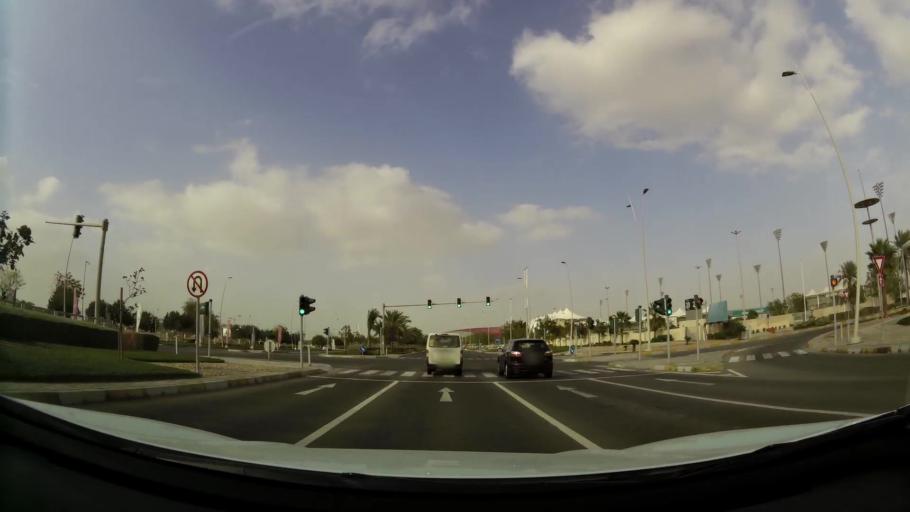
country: AE
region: Abu Dhabi
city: Abu Dhabi
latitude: 24.4754
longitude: 54.6027
